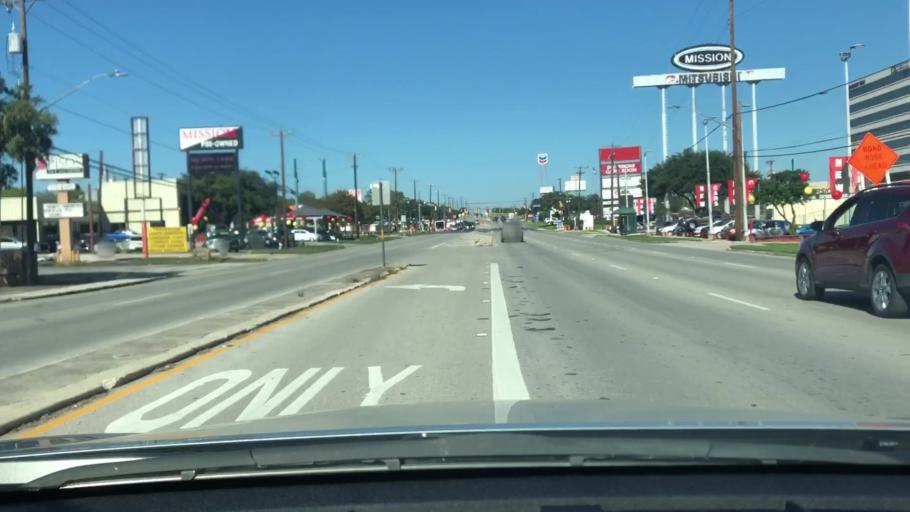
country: US
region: Texas
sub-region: Bexar County
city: Castle Hills
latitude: 29.5297
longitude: -98.4973
